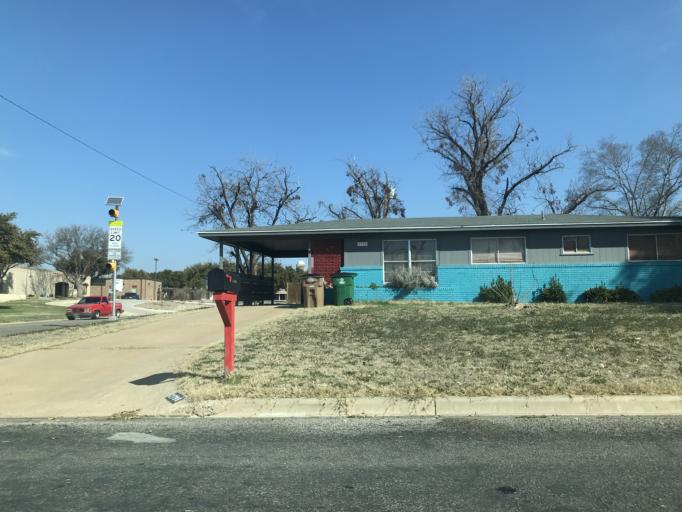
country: US
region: Texas
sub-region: Tom Green County
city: San Angelo
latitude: 31.4351
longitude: -100.4750
